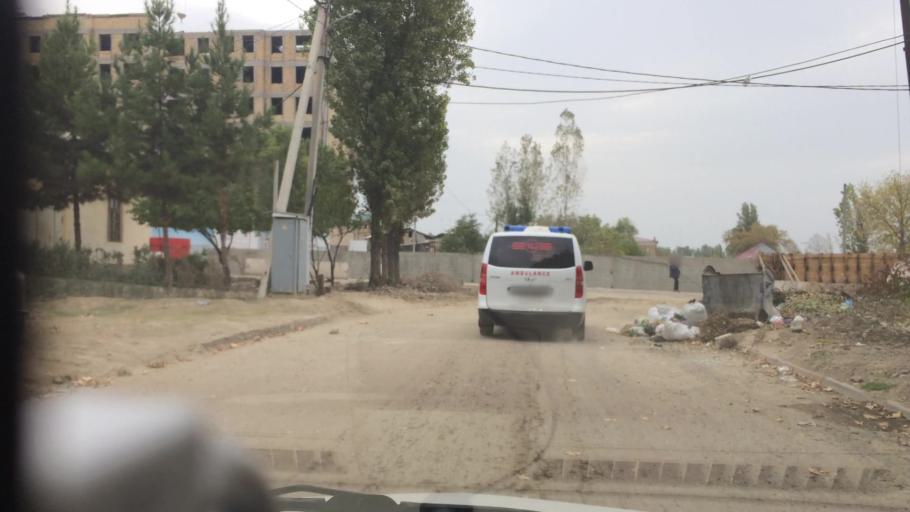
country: UZ
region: Toshkent
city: Salor
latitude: 41.3076
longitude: 69.3370
